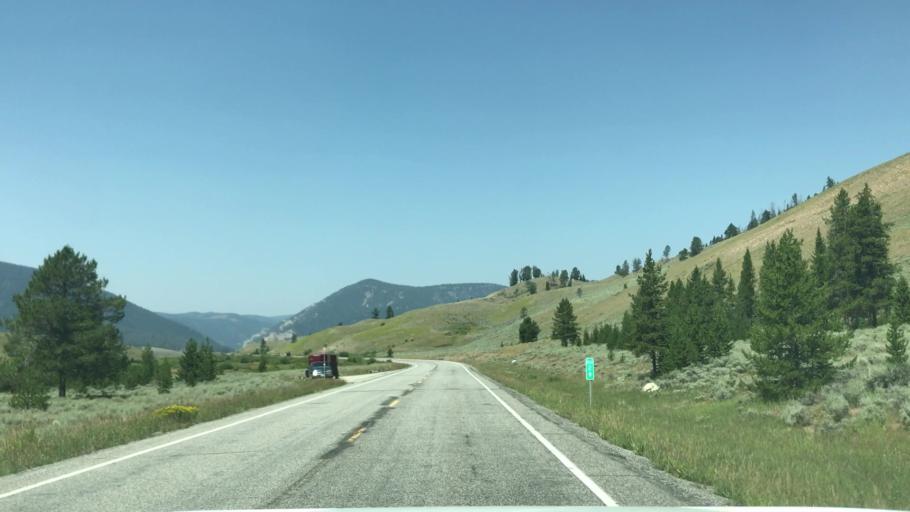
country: US
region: Montana
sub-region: Gallatin County
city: Big Sky
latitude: 45.0374
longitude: -111.1177
